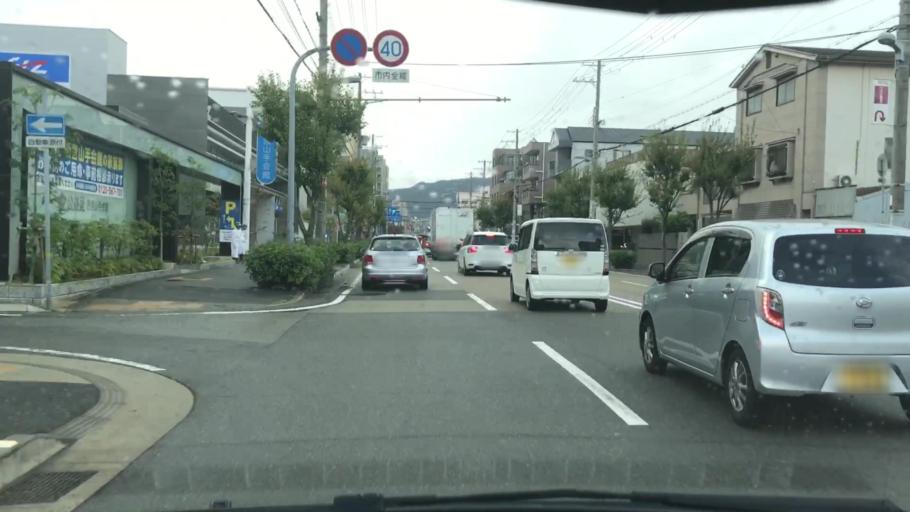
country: JP
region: Hyogo
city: Nishinomiya-hama
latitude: 34.7419
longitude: 135.3421
